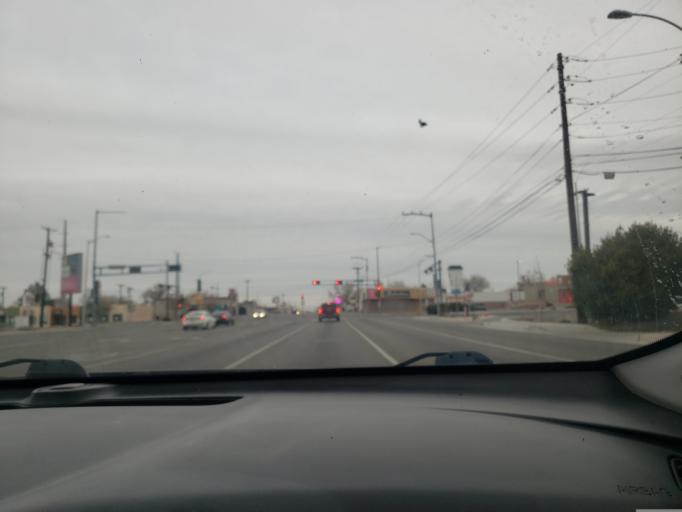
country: US
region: New Mexico
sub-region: Bernalillo County
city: Albuquerque
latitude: 35.1084
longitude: -106.5863
